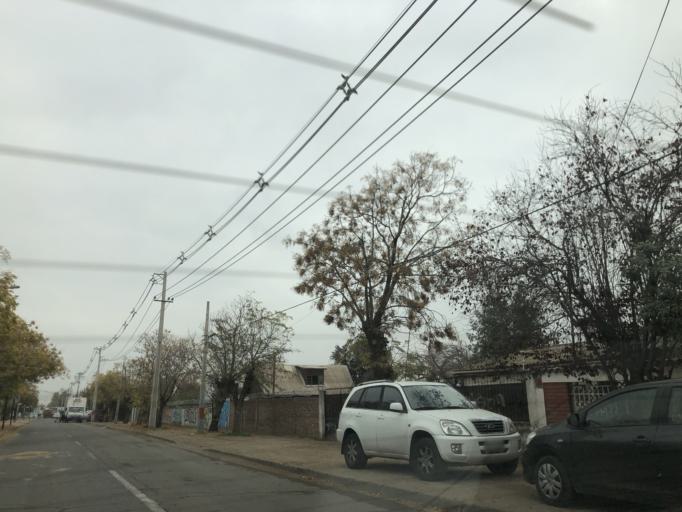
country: CL
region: Santiago Metropolitan
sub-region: Provincia de Santiago
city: La Pintana
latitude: -33.5805
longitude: -70.6078
